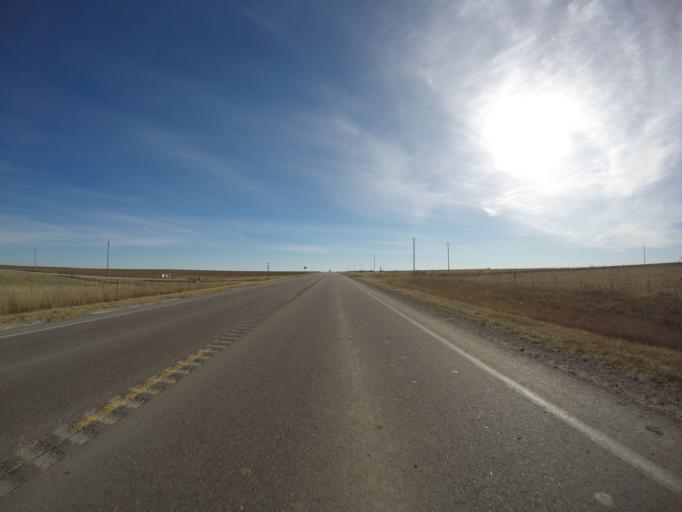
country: US
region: Kansas
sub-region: Marion County
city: Hillsboro
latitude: 38.4501
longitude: -97.2245
